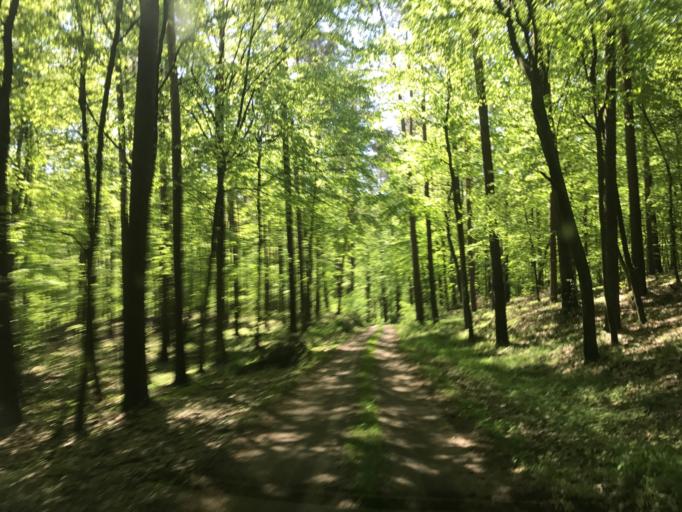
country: PL
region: Kujawsko-Pomorskie
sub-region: Powiat brodnicki
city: Gorzno
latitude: 53.2214
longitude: 19.7352
